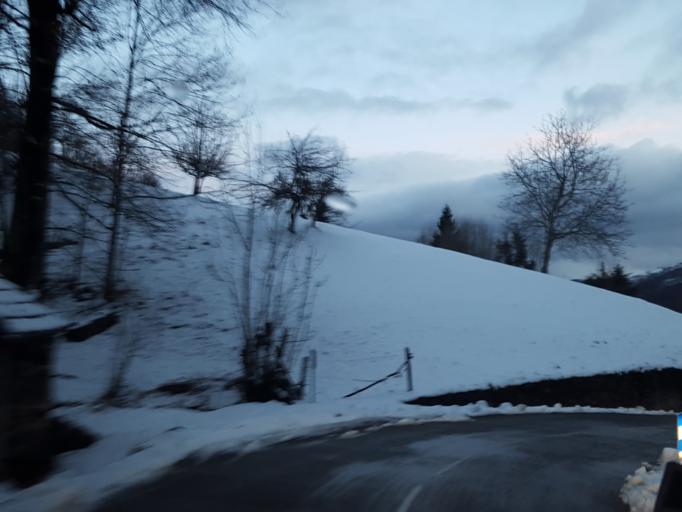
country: FR
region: Midi-Pyrenees
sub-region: Departement de l'Ariege
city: Tarascon-sur-Ariege
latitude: 42.8920
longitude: 1.4814
